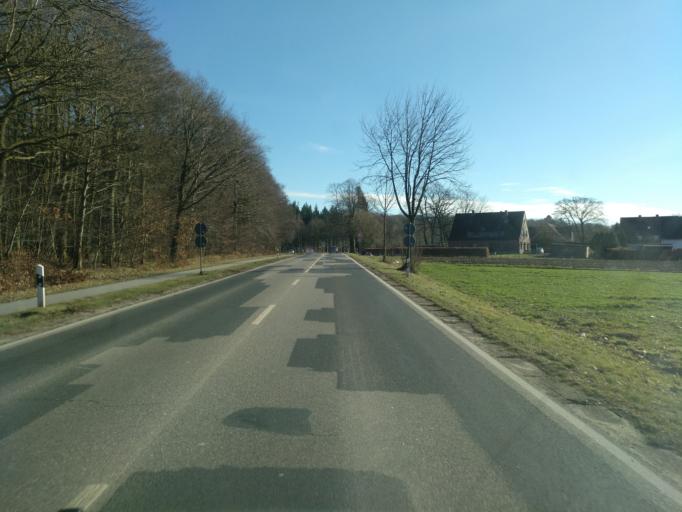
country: DE
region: Lower Saxony
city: Seevetal
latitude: 53.4351
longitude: 9.9182
